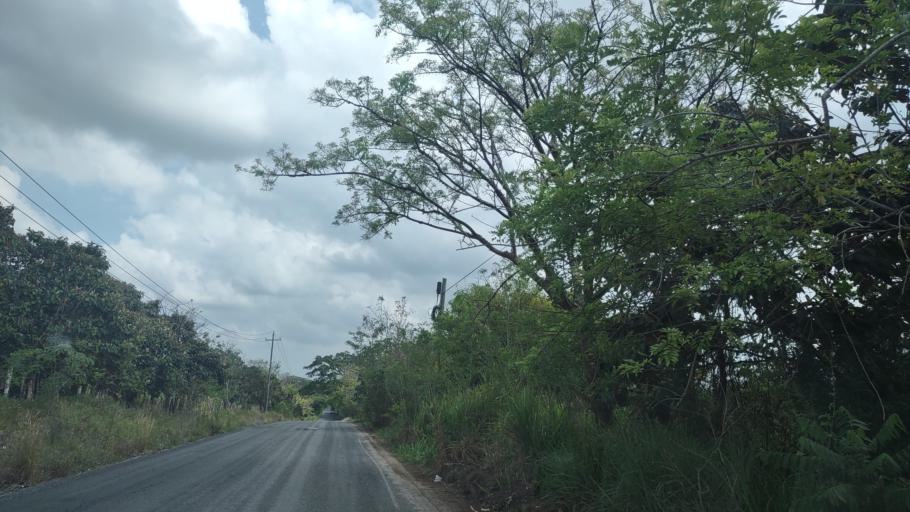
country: MX
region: Veracruz
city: Las Choapas
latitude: 17.9570
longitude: -94.1105
